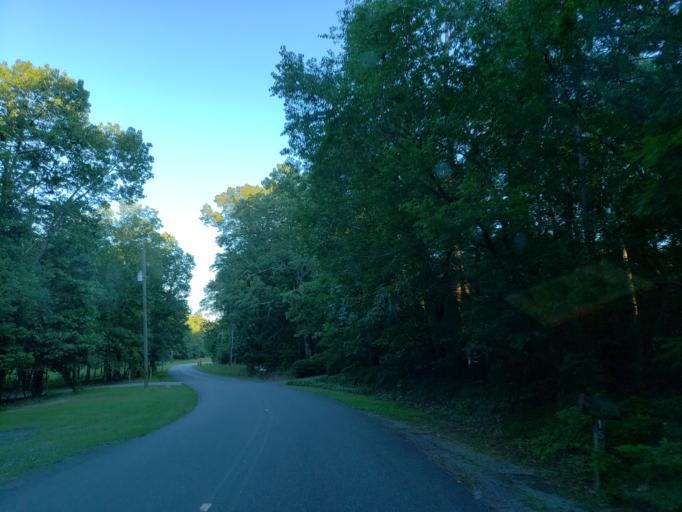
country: US
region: Georgia
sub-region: Bartow County
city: Euharlee
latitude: 34.0845
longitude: -84.9300
